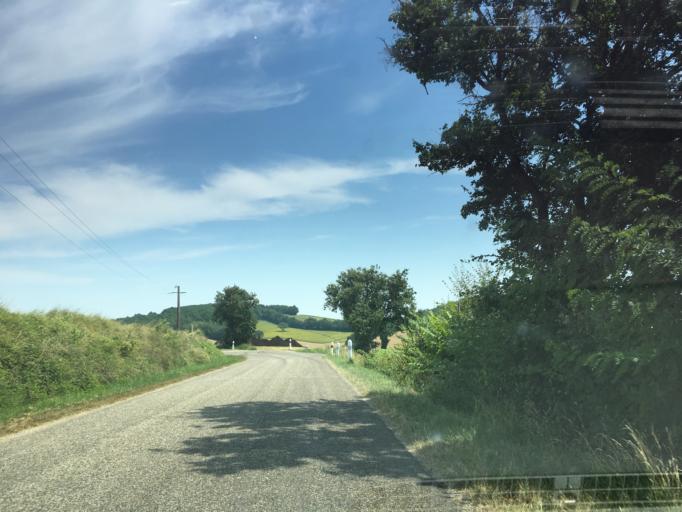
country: FR
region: Midi-Pyrenees
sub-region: Departement du Gers
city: Jegun
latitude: 43.8090
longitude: 0.5080
